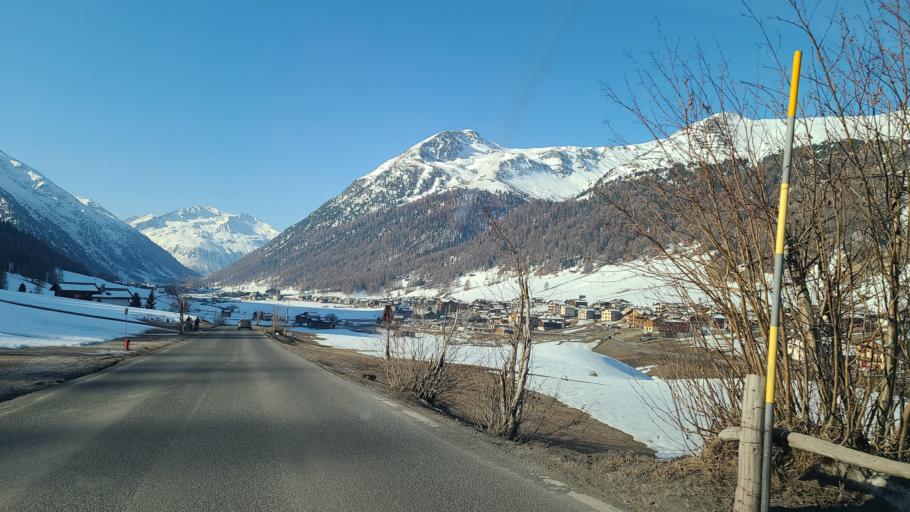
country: IT
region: Lombardy
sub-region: Provincia di Sondrio
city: Livigno
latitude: 46.5225
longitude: 10.1305
